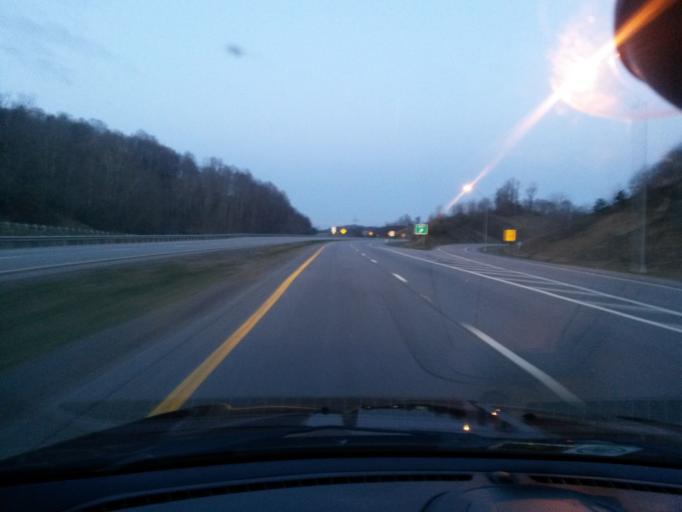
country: US
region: West Virginia
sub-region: Mercer County
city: Bluefield
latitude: 37.2746
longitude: -81.1568
